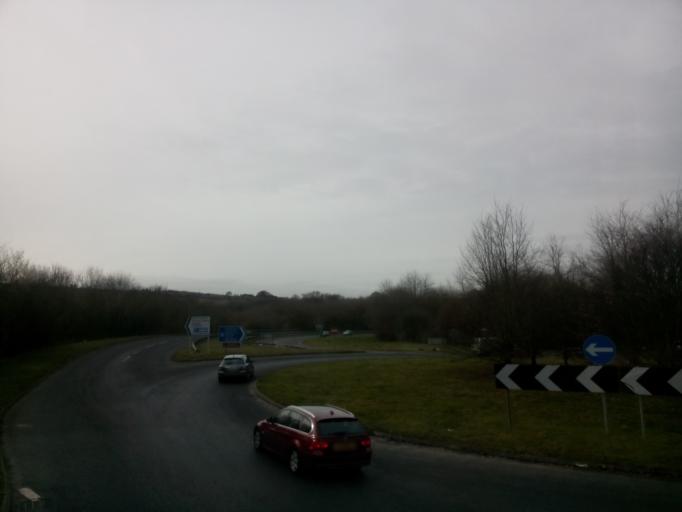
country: GB
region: England
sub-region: Hampshire
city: Winchester
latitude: 51.0519
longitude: -1.2975
